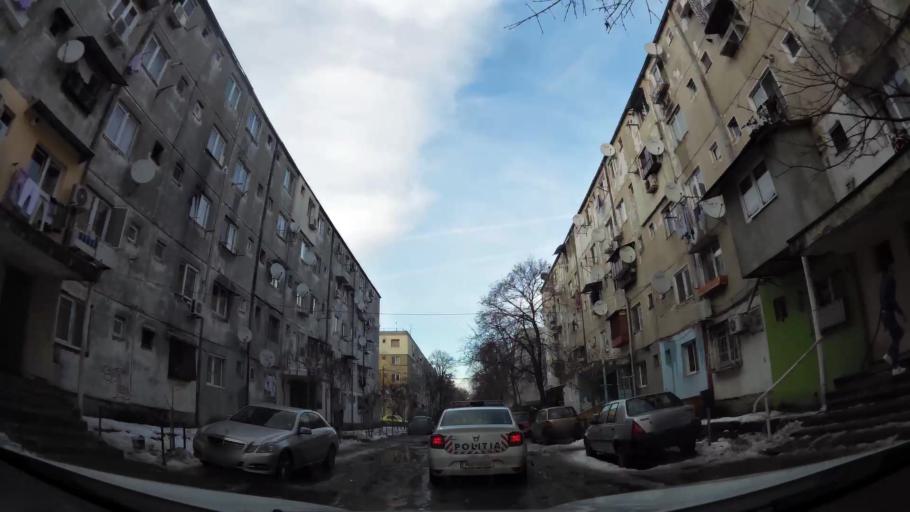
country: RO
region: Bucuresti
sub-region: Municipiul Bucuresti
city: Bucuresti
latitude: 44.3903
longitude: 26.0780
